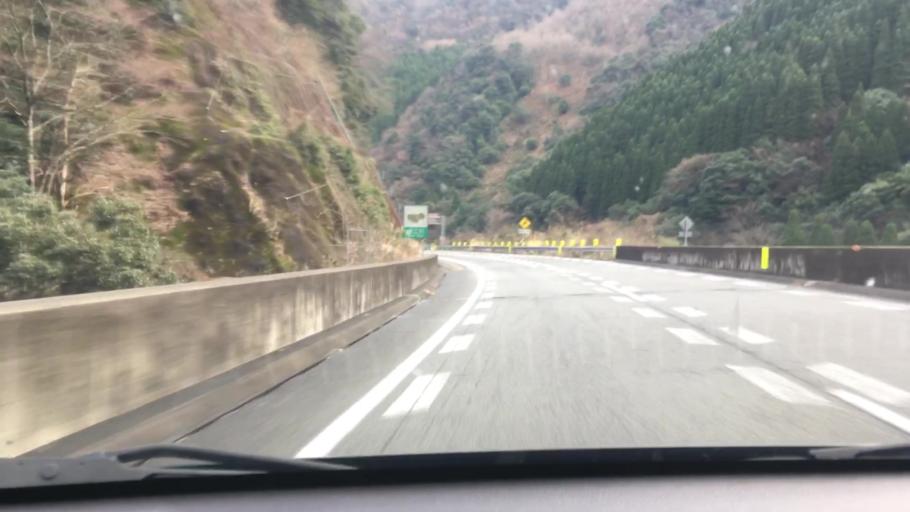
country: JP
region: Kumamoto
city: Hitoyoshi
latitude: 32.3330
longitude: 130.7391
